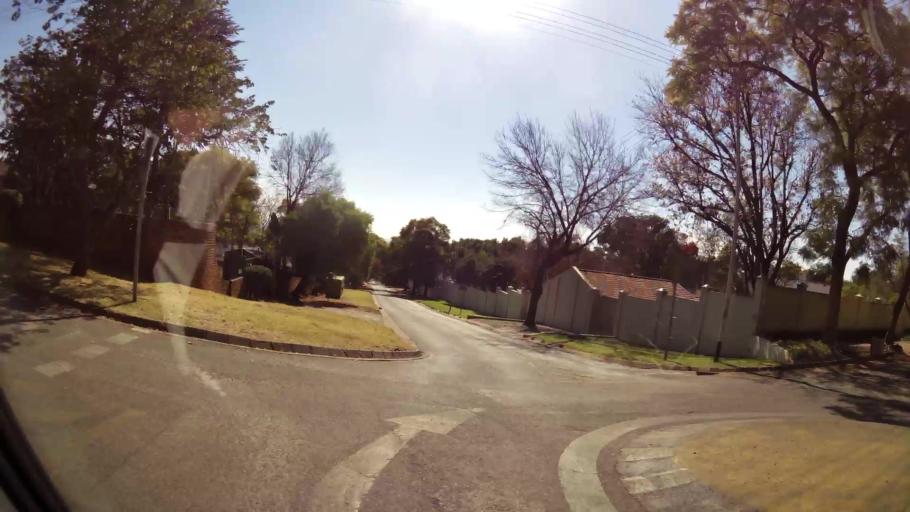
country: ZA
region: Gauteng
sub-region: City of Tshwane Metropolitan Municipality
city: Pretoria
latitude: -25.7834
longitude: 28.2450
